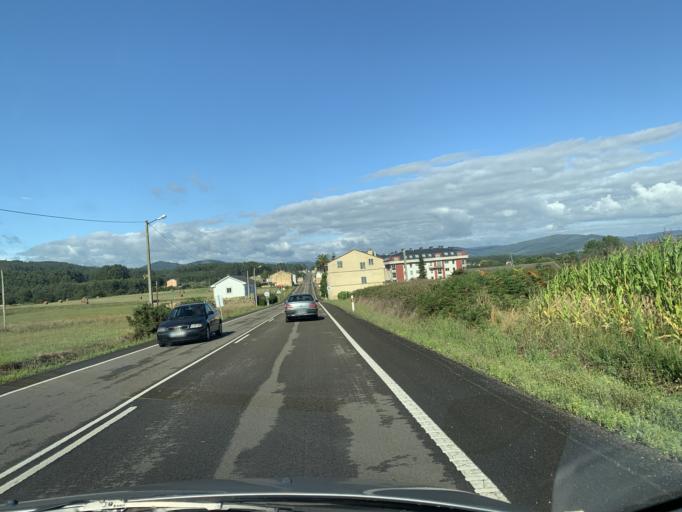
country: ES
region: Galicia
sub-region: Provincia de Lugo
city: Barreiros
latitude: 43.5454
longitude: -7.2030
